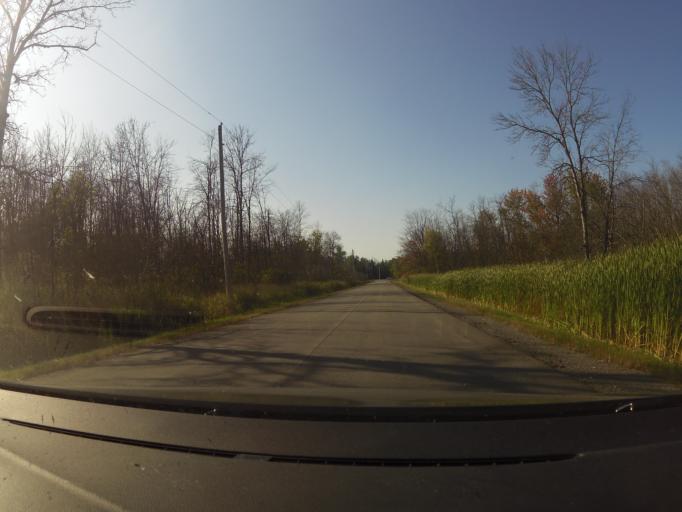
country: CA
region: Ontario
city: Carleton Place
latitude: 45.2910
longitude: -76.0859
